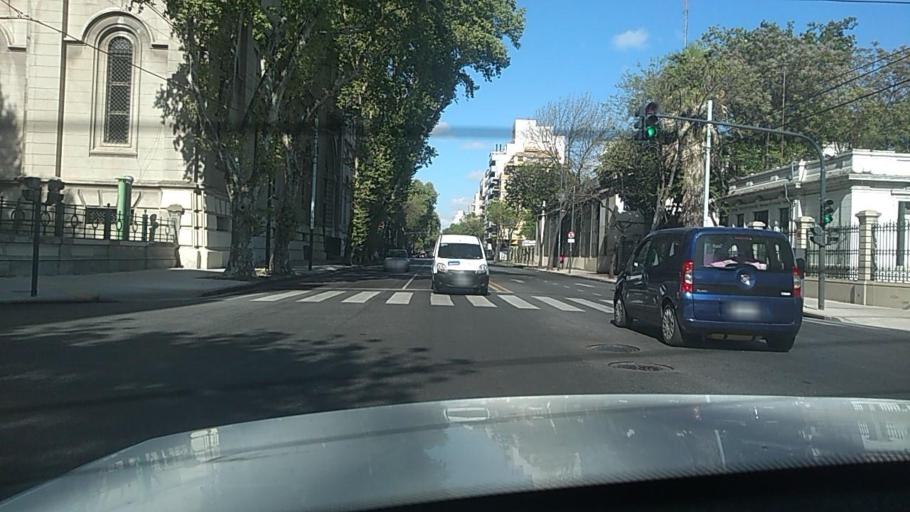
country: AR
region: Buenos Aires F.D.
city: Villa Santa Rita
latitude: -34.6042
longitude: -58.5091
